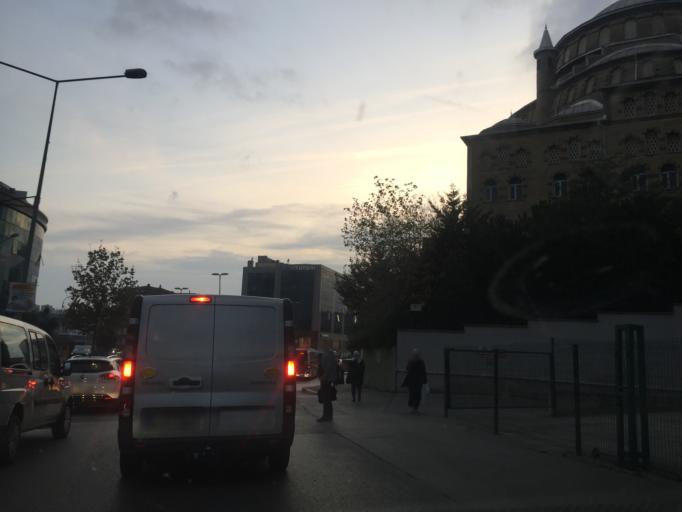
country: TR
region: Istanbul
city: Samandira
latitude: 40.9817
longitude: 29.2211
